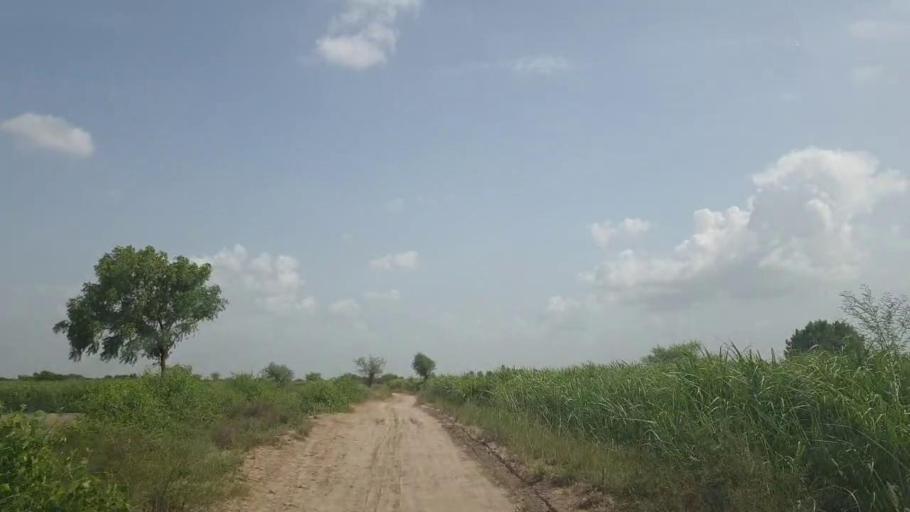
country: PK
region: Sindh
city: Tando Bago
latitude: 24.7475
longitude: 69.1786
